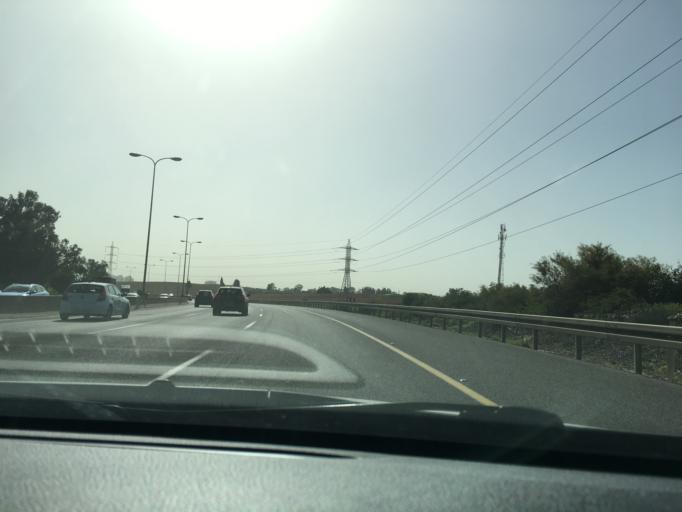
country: IL
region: Central District
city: Hod HaSharon
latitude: 32.1569
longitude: 34.8736
